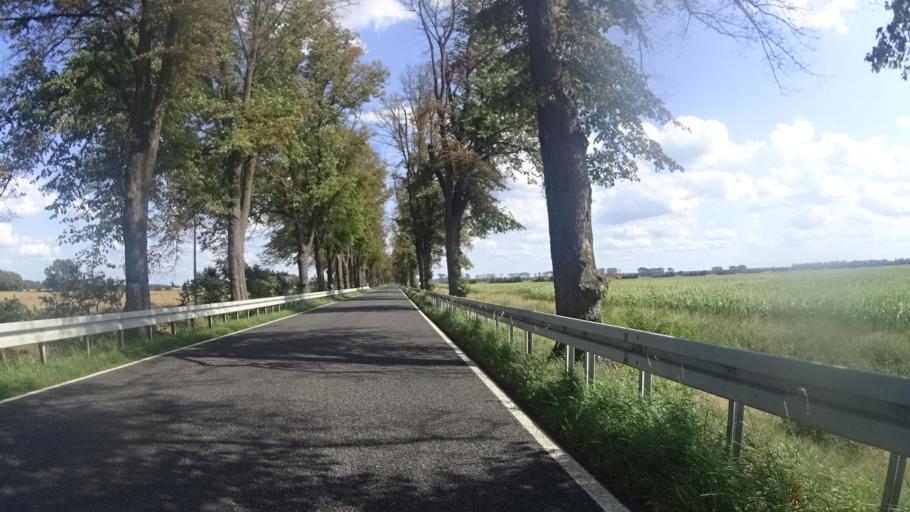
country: DE
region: Brandenburg
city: Rhinow
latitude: 52.7720
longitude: 12.2622
